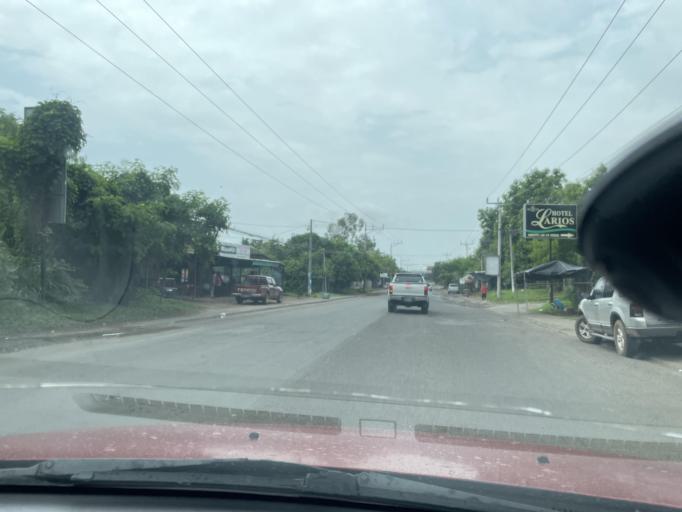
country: SV
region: La Union
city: Santa Rosa de Lima
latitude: 13.6303
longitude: -87.8867
